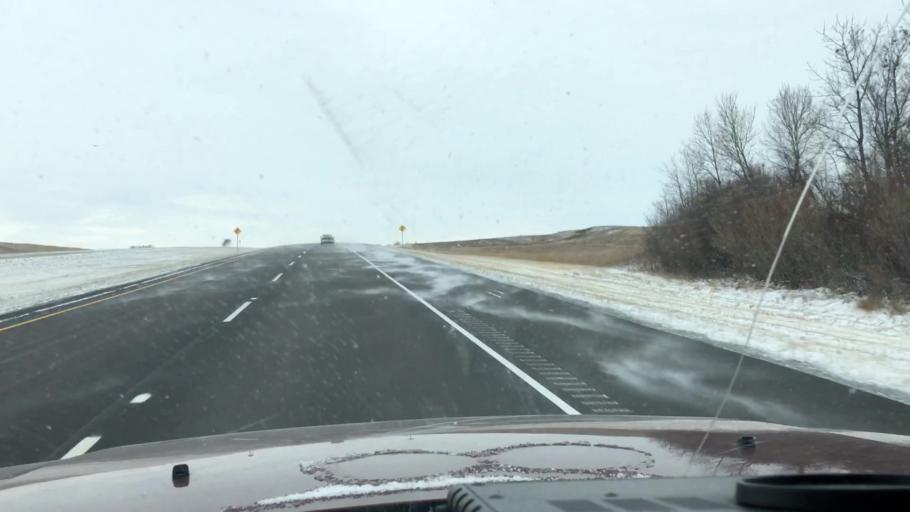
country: CA
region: Saskatchewan
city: Saskatoon
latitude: 51.7236
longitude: -106.4719
